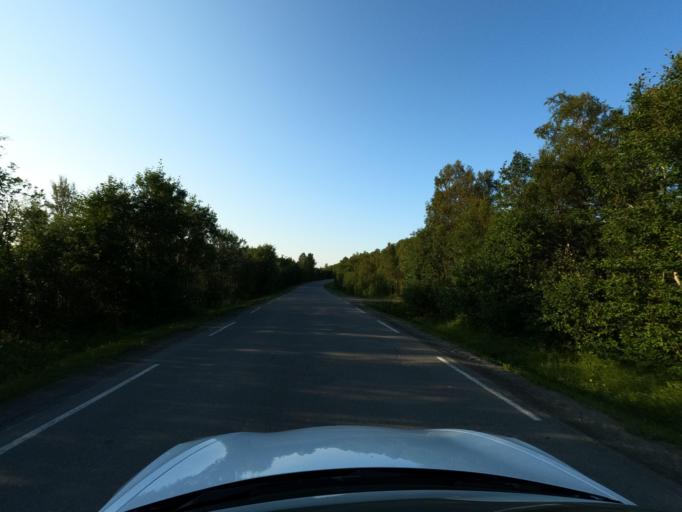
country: NO
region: Troms
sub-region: Skanland
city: Evenskjer
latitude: 68.4848
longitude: 16.7117
